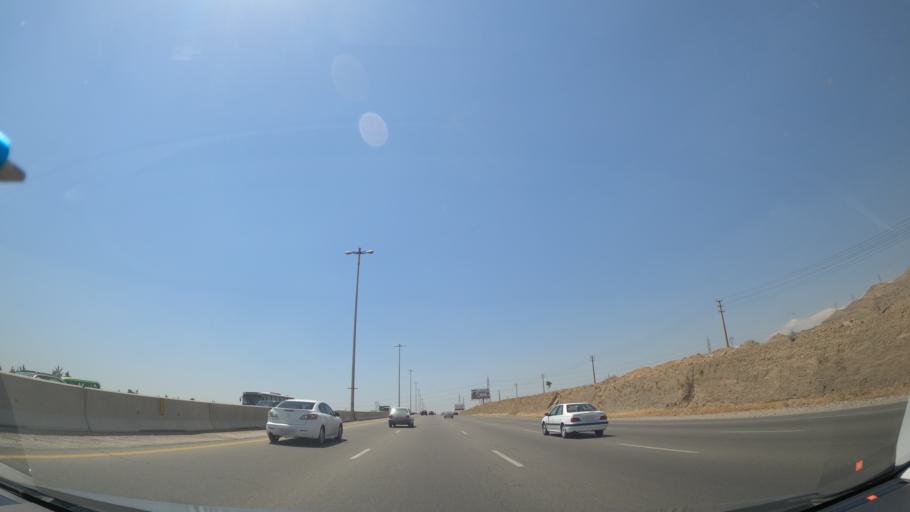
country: IR
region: Tehran
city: Shahr-e Qods
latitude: 35.7678
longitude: 51.0514
